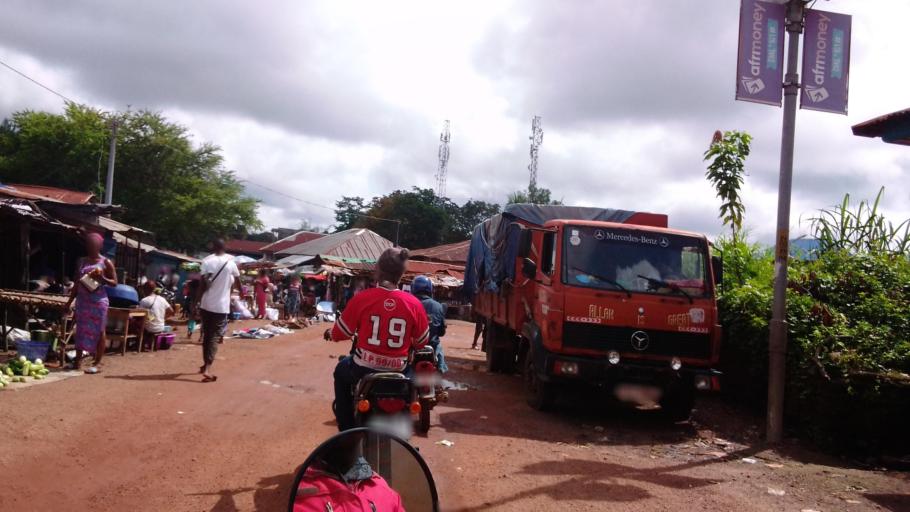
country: SL
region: Northern Province
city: Makeni
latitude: 8.8903
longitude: -12.0415
